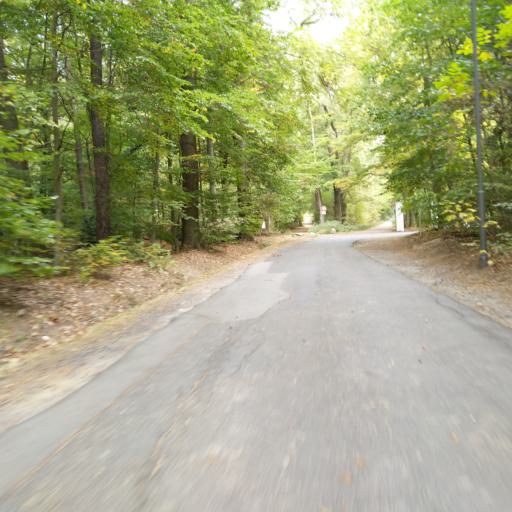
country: DE
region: Hesse
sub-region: Regierungsbezirk Darmstadt
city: Bad Homburg vor der Hoehe
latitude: 50.2372
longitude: 8.6233
